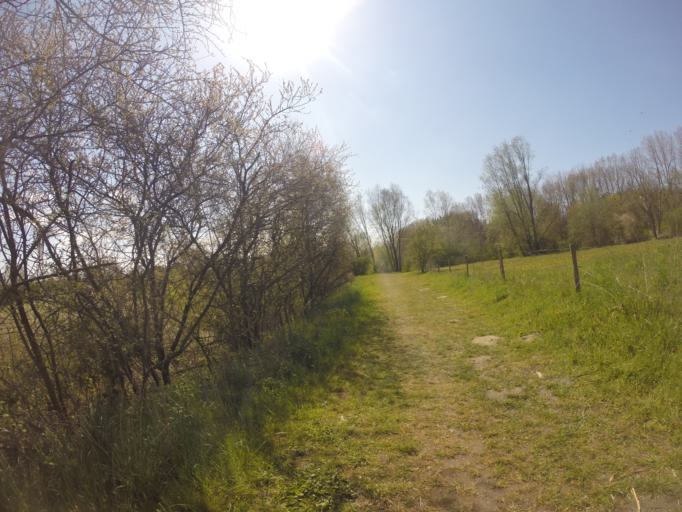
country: BE
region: Flanders
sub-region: Provincie West-Vlaanderen
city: Oostkamp
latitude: 51.1586
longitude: 3.2568
